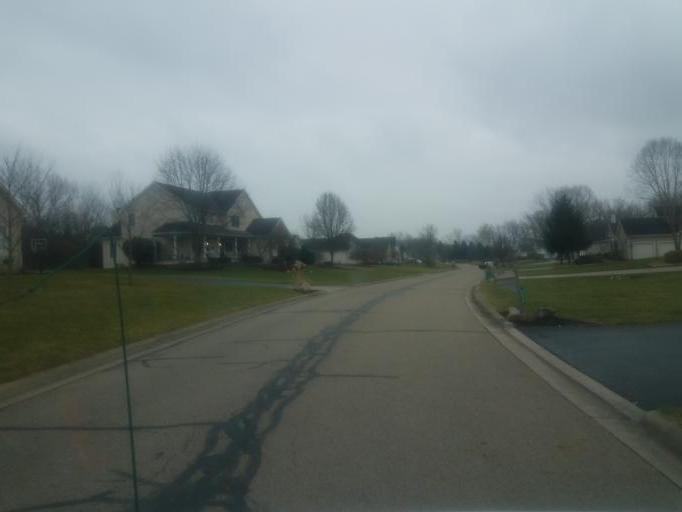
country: US
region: Ohio
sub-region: Delaware County
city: Lewis Center
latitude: 40.1796
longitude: -82.9578
